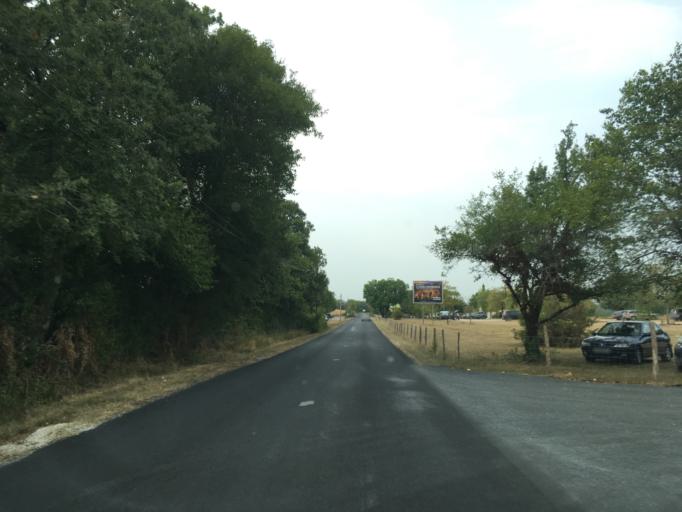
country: FR
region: Midi-Pyrenees
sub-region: Departement du Lot
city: Souillac
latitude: 44.8288
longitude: 1.5678
